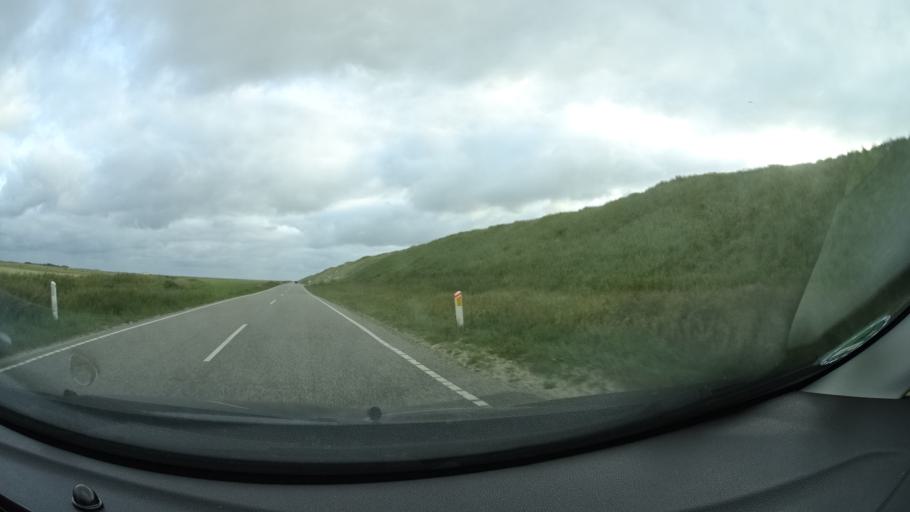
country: DK
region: Central Jutland
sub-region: Lemvig Kommune
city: Harboore
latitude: 56.4512
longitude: 8.1255
